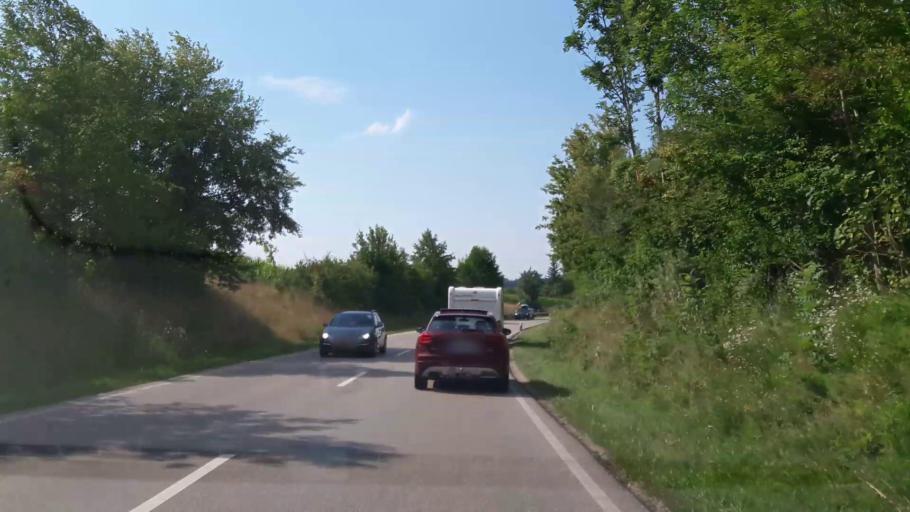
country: DE
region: Bavaria
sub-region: Upper Bavaria
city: Teisendorf
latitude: 47.8440
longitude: 12.8149
